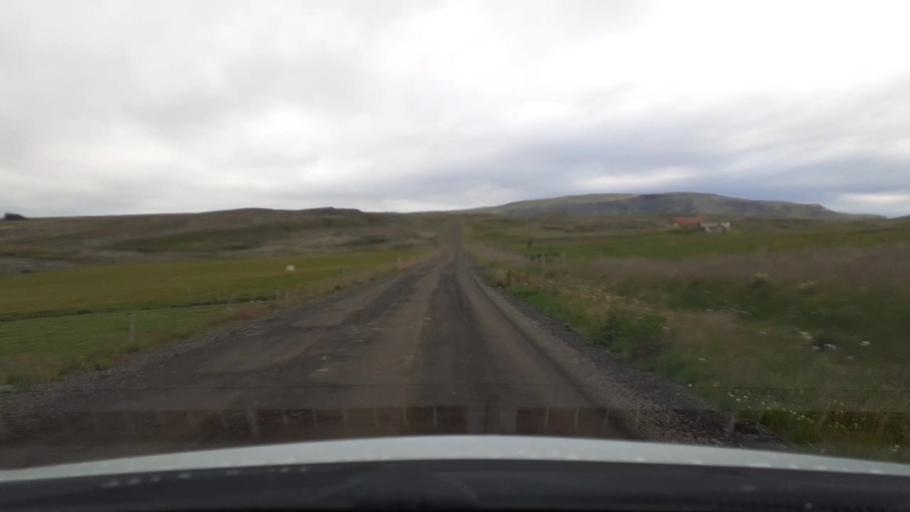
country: IS
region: Capital Region
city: Mosfellsbaer
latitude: 64.2033
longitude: -21.5606
